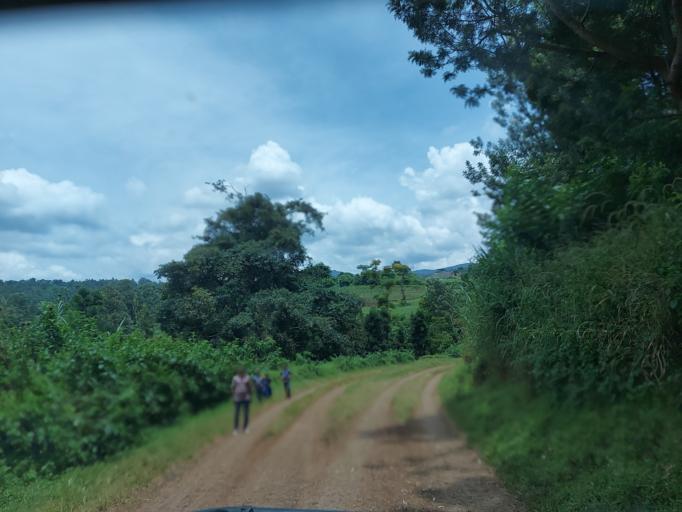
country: CD
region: South Kivu
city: Kabare
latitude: -2.3371
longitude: 28.7849
